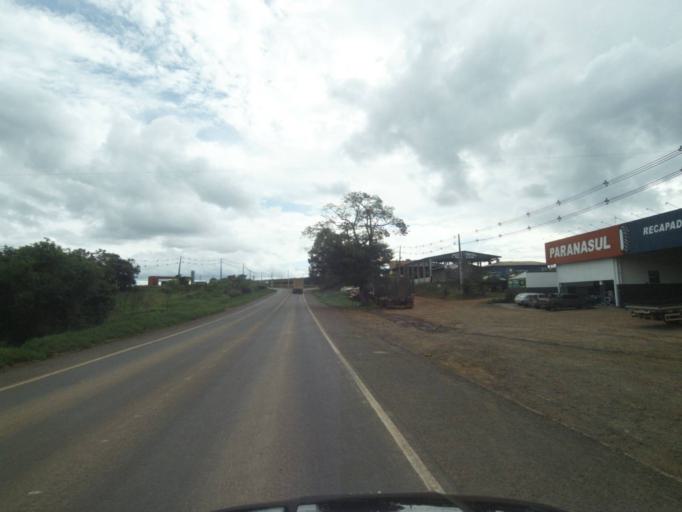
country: BR
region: Parana
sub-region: Telemaco Borba
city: Telemaco Borba
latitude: -24.3829
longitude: -50.6733
